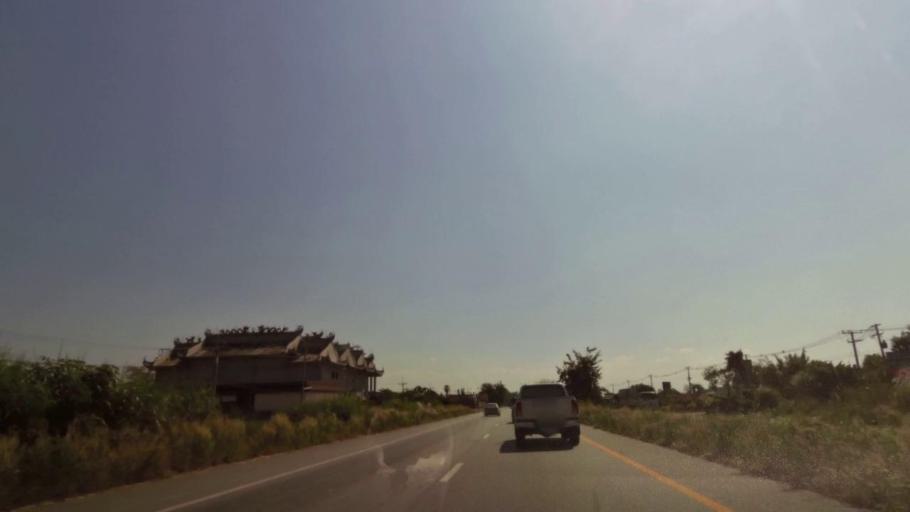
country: TH
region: Nakhon Sawan
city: Kao Liao
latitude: 15.8283
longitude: 100.1187
